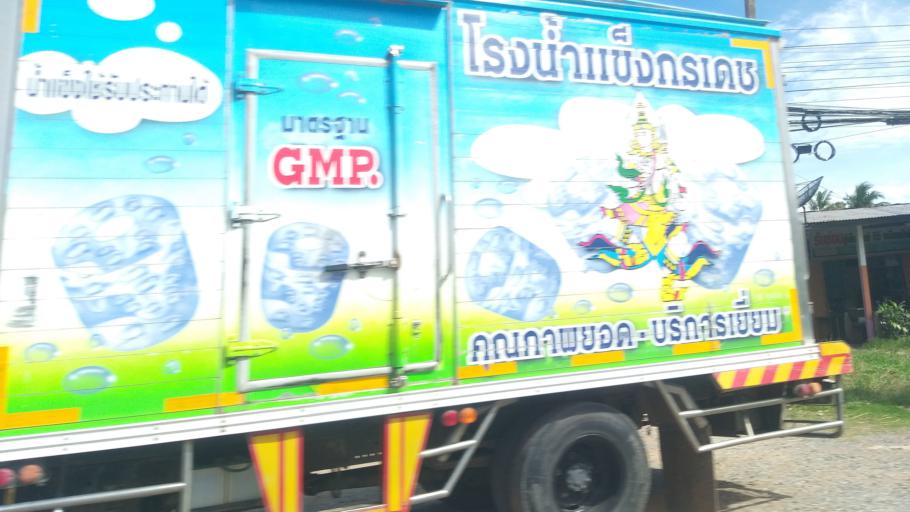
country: TH
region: Chaiyaphum
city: Ban Thaen
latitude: 16.4060
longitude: 102.3450
